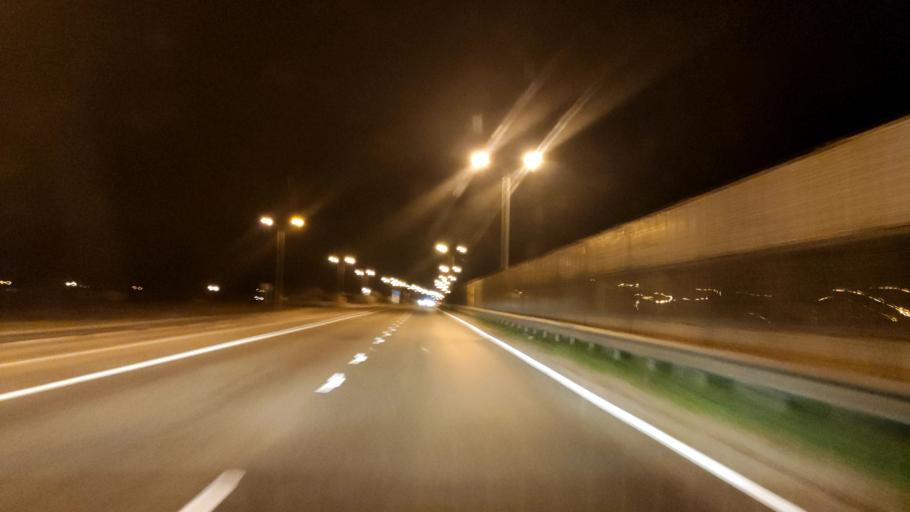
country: RU
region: Belgorod
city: Staryy Oskol
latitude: 51.3419
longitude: 37.8040
